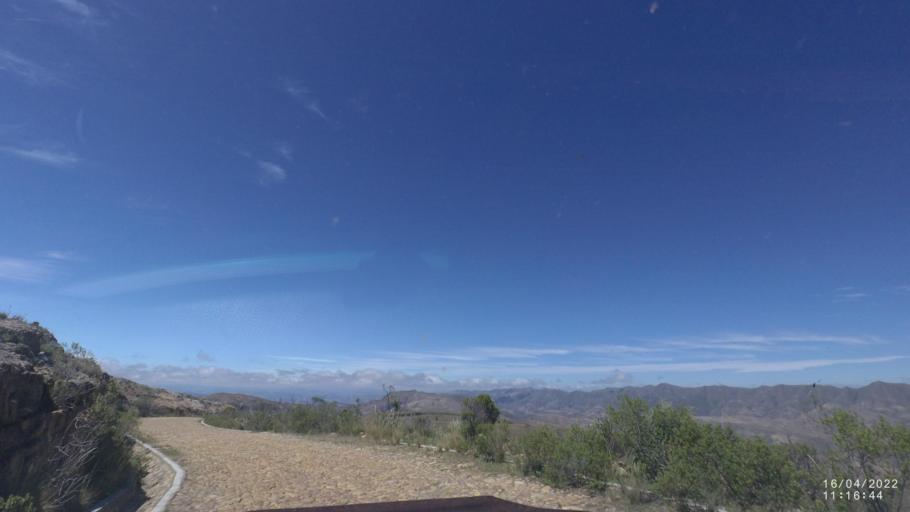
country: BO
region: Cochabamba
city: Arani
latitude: -17.8877
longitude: -65.6990
